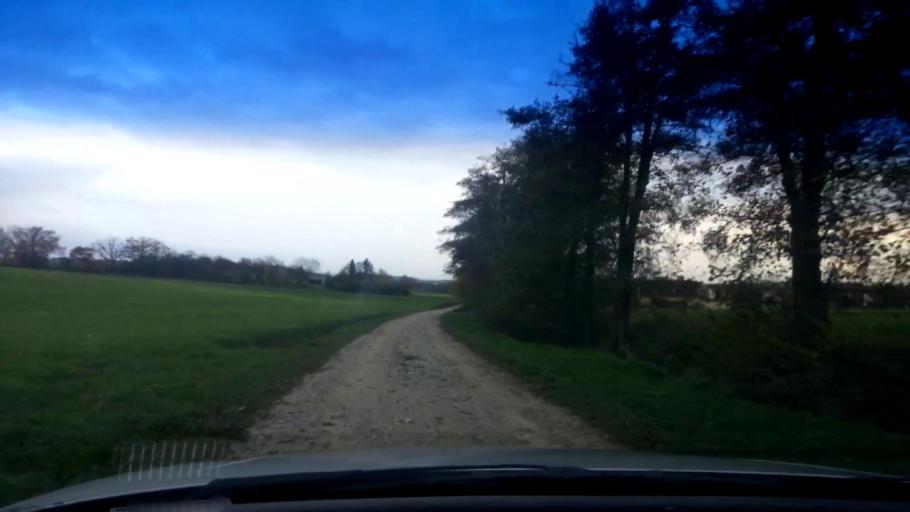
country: DE
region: Bavaria
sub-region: Upper Franconia
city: Memmelsdorf
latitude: 49.9620
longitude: 10.9615
